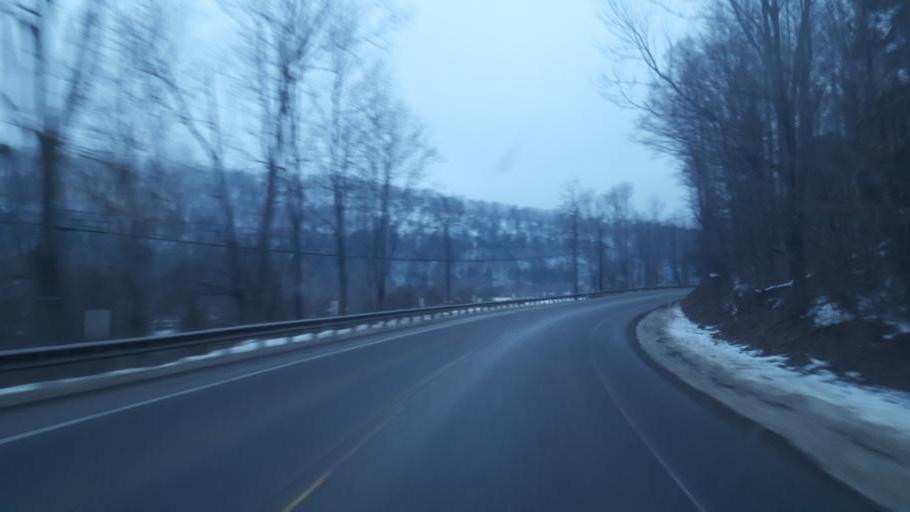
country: US
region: Pennsylvania
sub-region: Potter County
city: Coudersport
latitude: 41.7526
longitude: -78.0544
